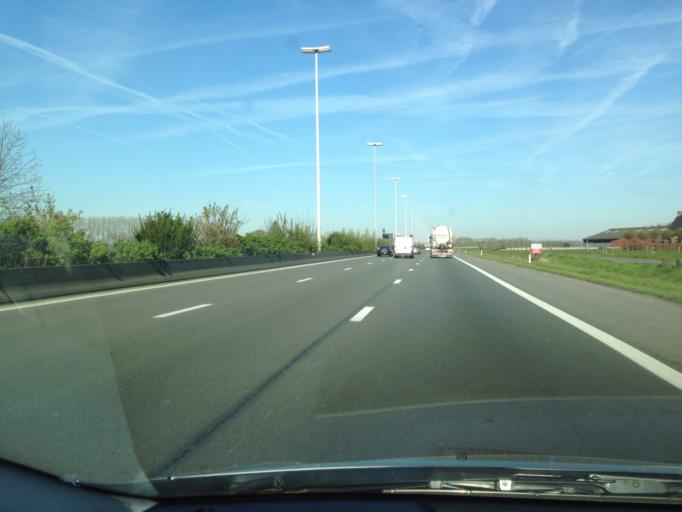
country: BE
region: Flanders
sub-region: Provincie West-Vlaanderen
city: Beernem
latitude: 51.1298
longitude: 3.2934
